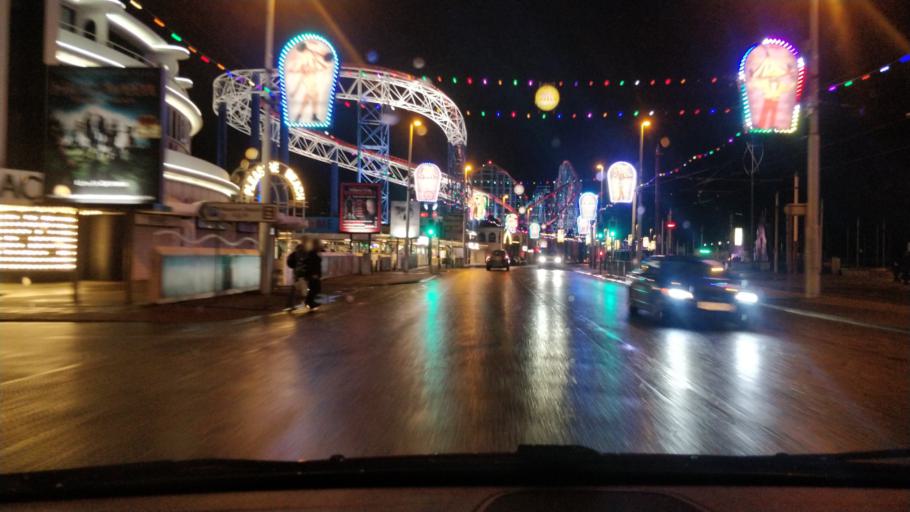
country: GB
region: England
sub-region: Blackpool
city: Blackpool
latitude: 53.7938
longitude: -3.0563
